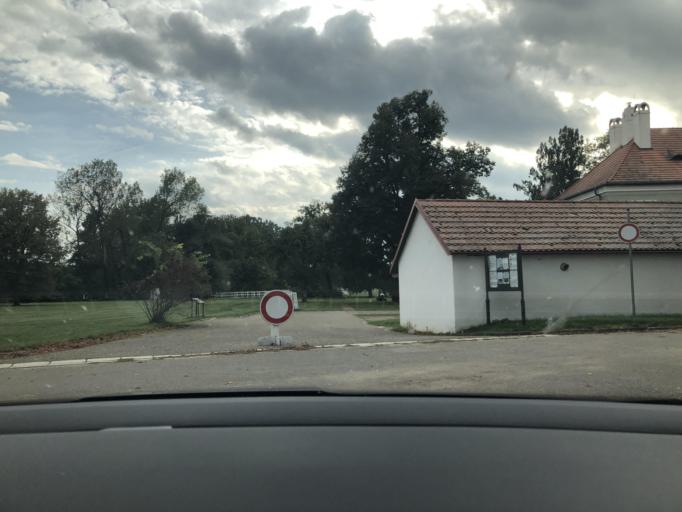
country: CZ
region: Pardubicky
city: Recany nad Labem
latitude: 50.0572
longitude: 15.4866
